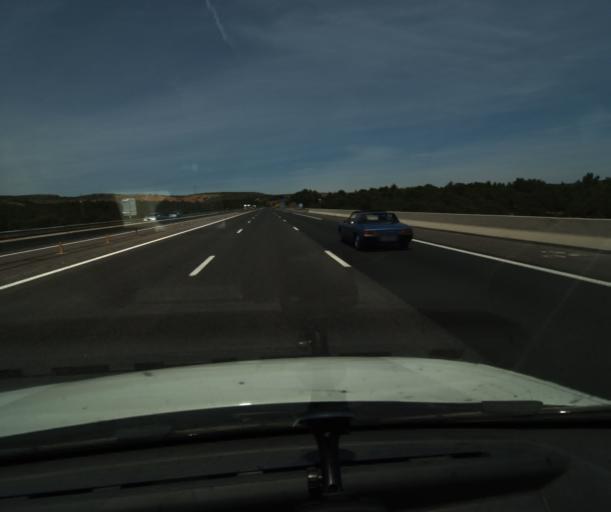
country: FR
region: Languedoc-Roussillon
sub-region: Departement des Pyrenees-Orientales
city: Salses-le-Chateau
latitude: 42.8311
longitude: 2.9102
